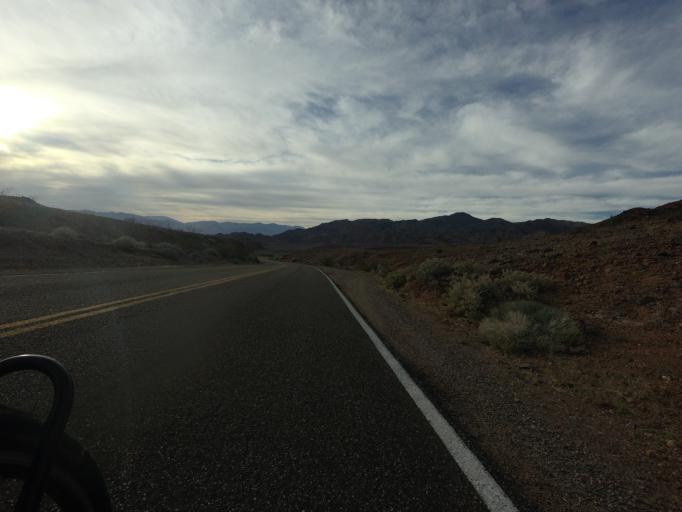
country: US
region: California
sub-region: San Bernardino County
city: Fort Irwin
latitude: 35.9101
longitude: -116.5793
